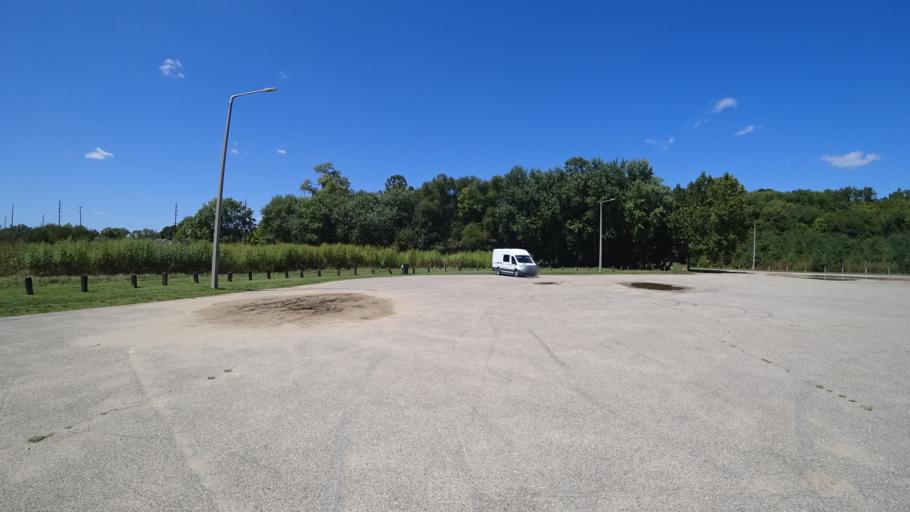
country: US
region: Ohio
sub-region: Butler County
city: Hamilton
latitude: 39.4147
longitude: -84.5543
